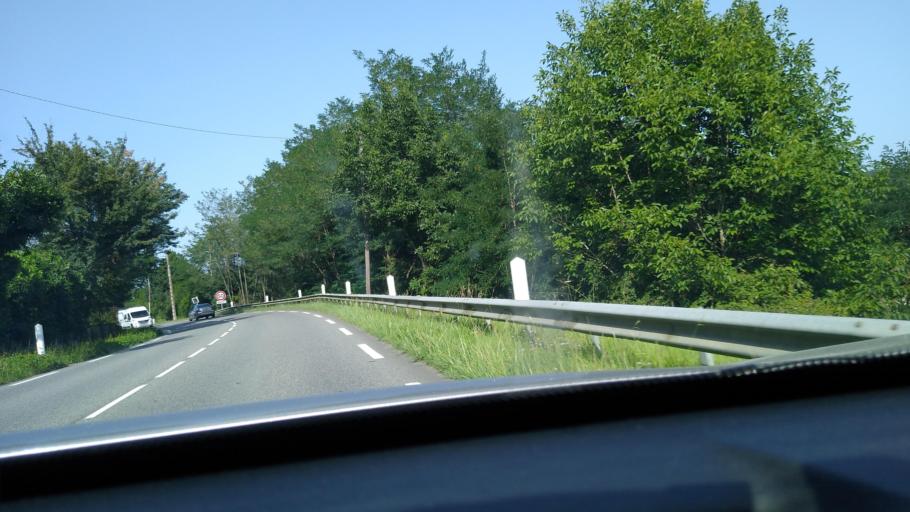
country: FR
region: Midi-Pyrenees
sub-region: Departement de la Haute-Garonne
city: Salies-du-Salat
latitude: 43.0953
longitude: 0.9526
